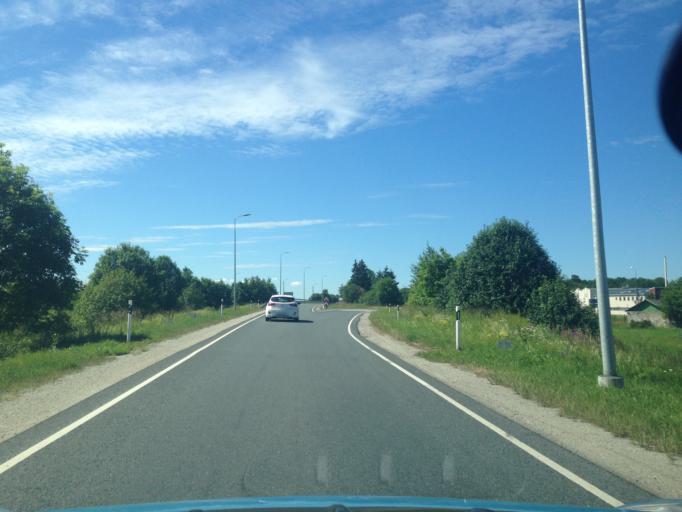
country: EE
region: Harju
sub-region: Saue linn
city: Saue
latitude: 59.3149
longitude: 24.5740
